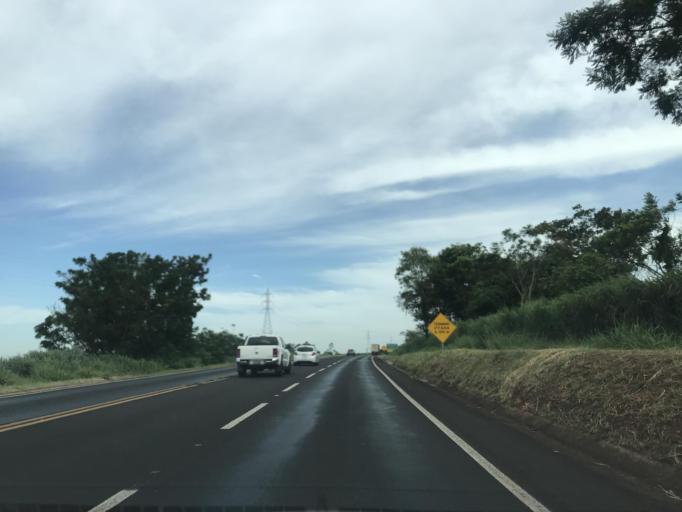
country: BR
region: Parana
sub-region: Paranavai
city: Nova Aurora
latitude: -22.9939
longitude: -52.5894
